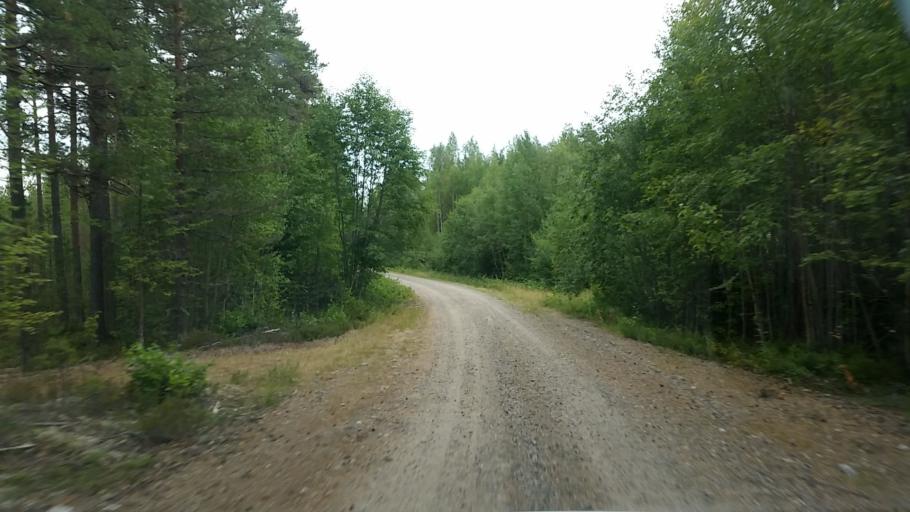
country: SE
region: Gaevleborg
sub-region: Ljusdals Kommun
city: Farila
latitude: 61.8181
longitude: 15.8494
